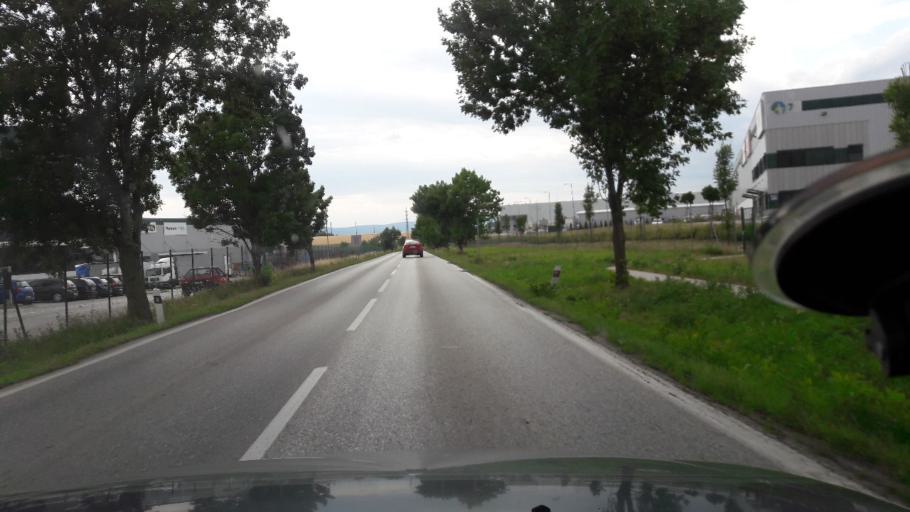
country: SK
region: Bratislavsky
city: Senec
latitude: 48.2448
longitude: 17.3527
